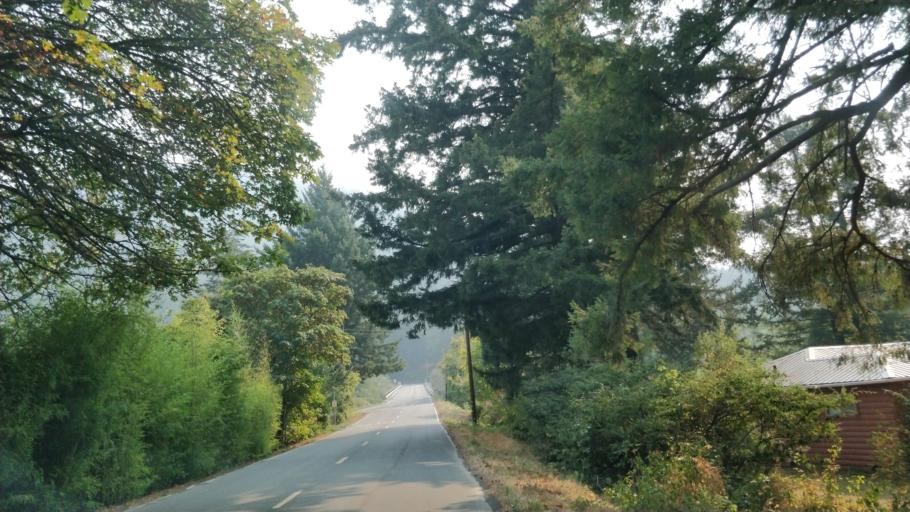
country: US
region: California
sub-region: Humboldt County
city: Rio Dell
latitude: 40.3155
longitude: -124.2832
